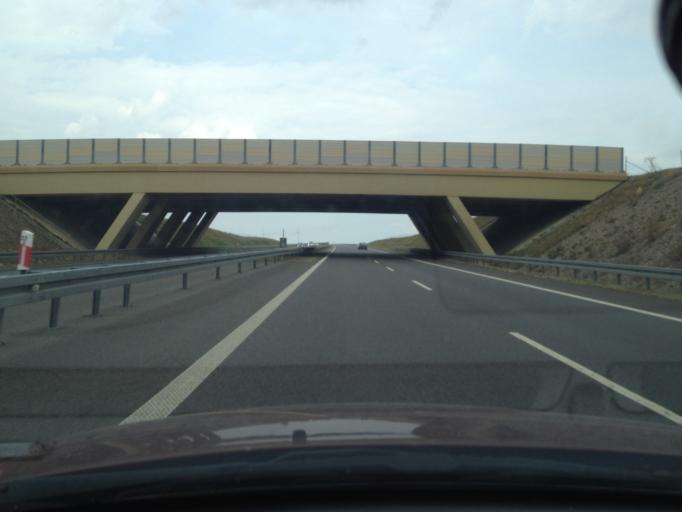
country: PL
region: West Pomeranian Voivodeship
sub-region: Powiat pyrzycki
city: Kozielice
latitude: 53.0663
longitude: 14.8623
